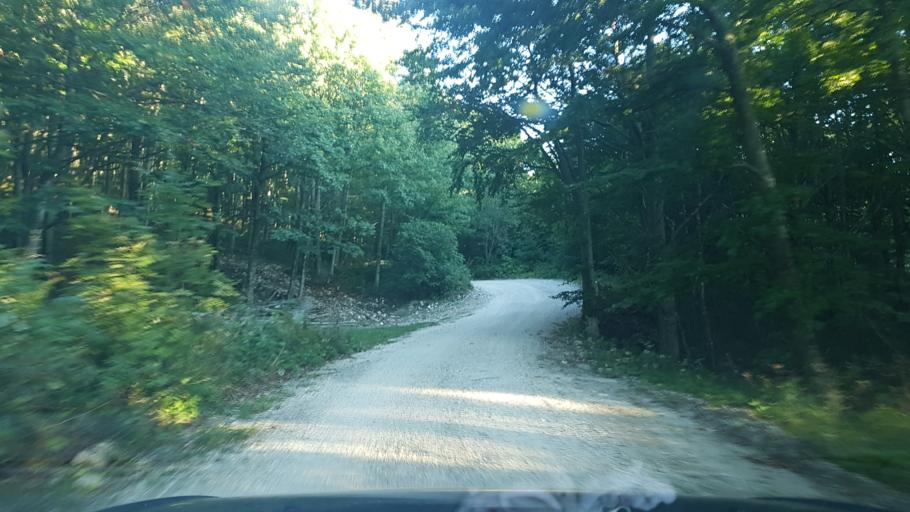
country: SI
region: Vipava
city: Vipava
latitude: 45.7764
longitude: 14.0483
